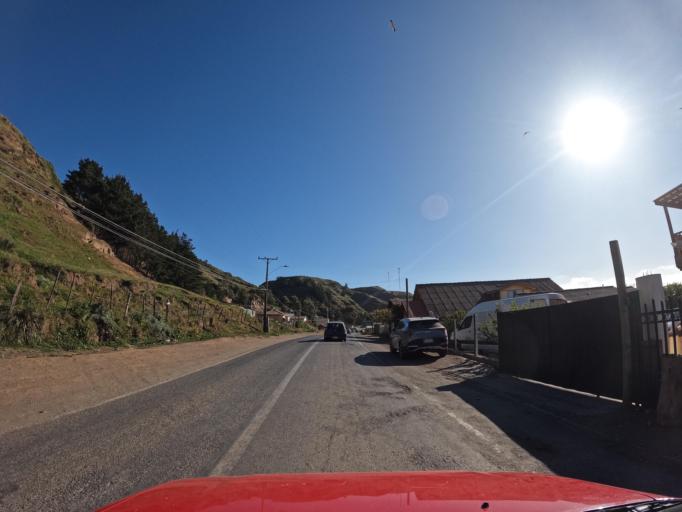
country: CL
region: Maule
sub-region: Provincia de Talca
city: Constitucion
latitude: -34.8836
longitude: -72.1589
